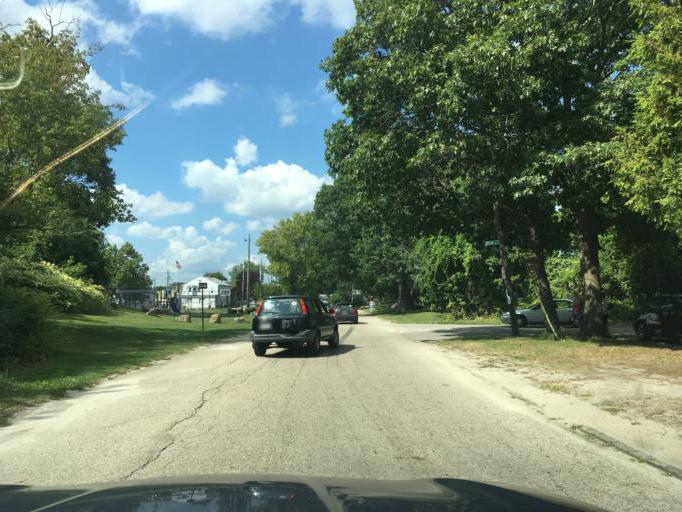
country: US
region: Rhode Island
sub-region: Kent County
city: Warwick
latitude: 41.6855
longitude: -71.3972
